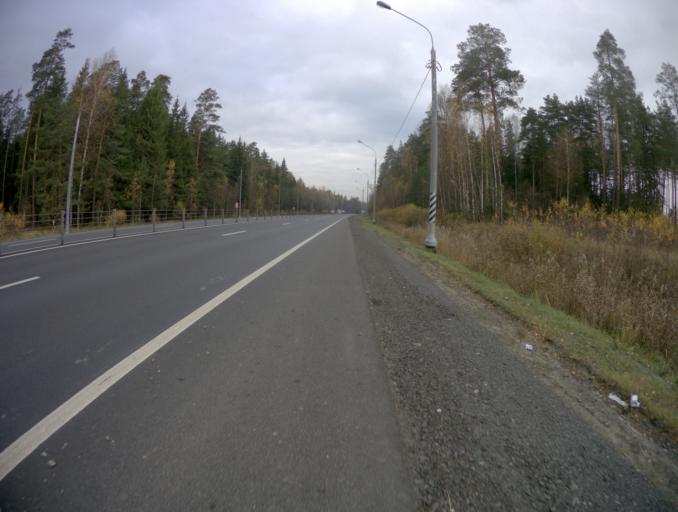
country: RU
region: Moskovskaya
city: Malaya Dubna
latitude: 55.8541
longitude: 38.9629
